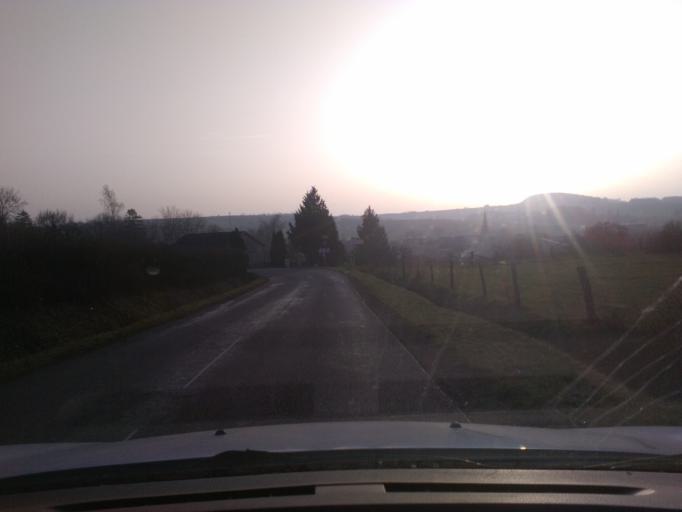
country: FR
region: Lorraine
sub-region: Departement des Vosges
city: Vittel
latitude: 48.2550
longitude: 6.0010
